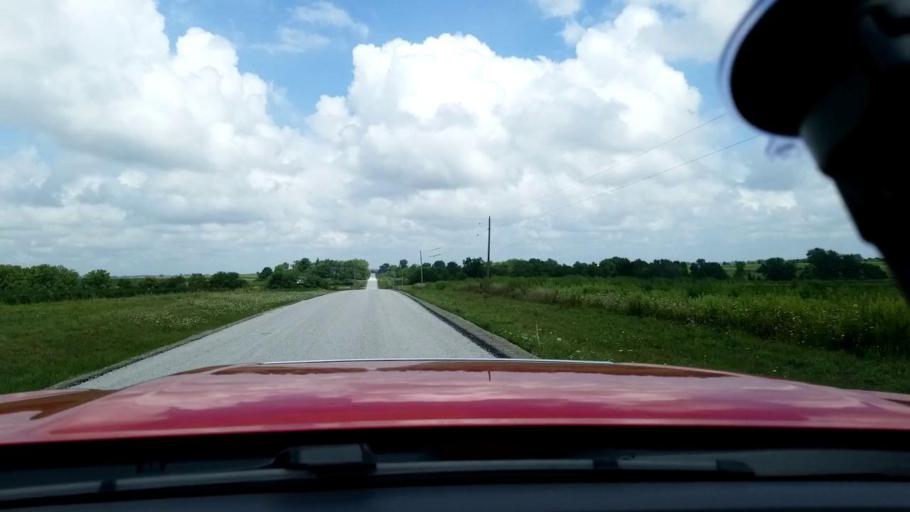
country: US
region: Iowa
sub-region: Decatur County
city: Lamoni
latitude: 40.6282
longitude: -94.0533
